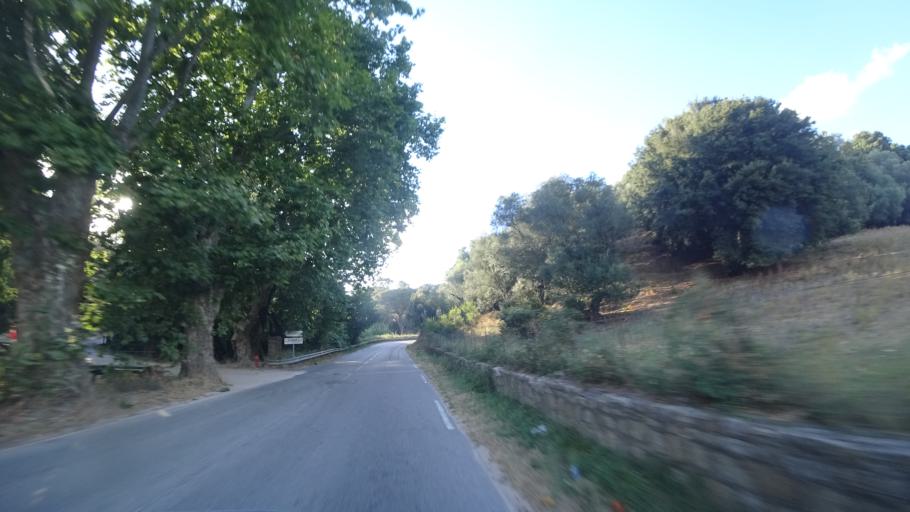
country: FR
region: Corsica
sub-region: Departement de la Corse-du-Sud
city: Ajaccio
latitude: 41.9514
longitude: 8.7329
